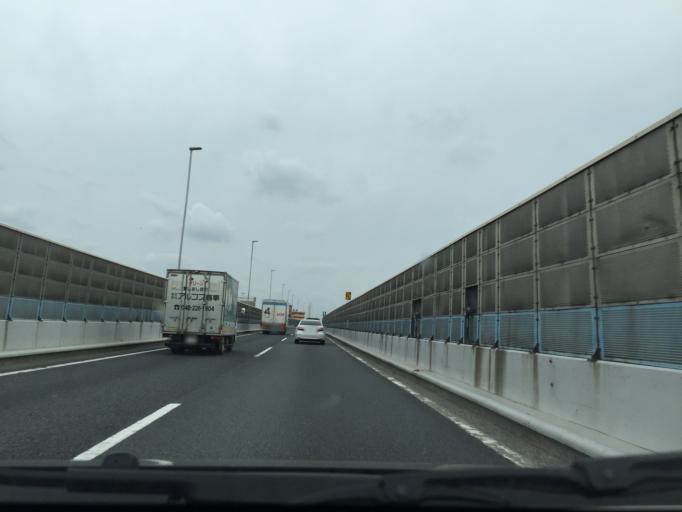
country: JP
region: Saitama
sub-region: Kawaguchi-shi
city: Hatogaya-honcho
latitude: 35.8203
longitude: 139.7601
